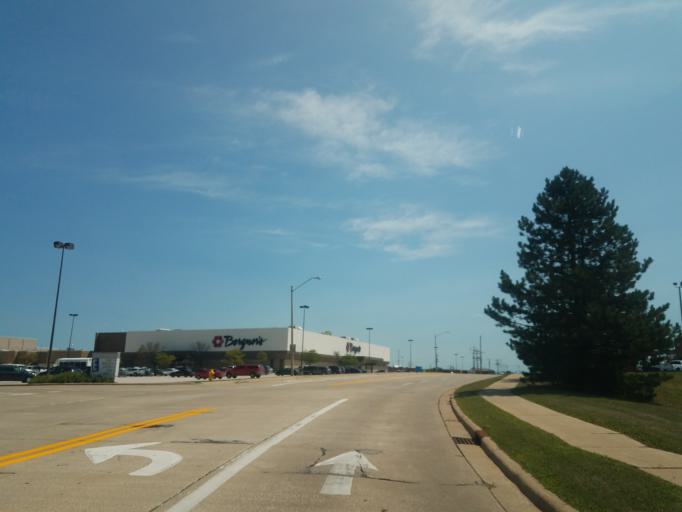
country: US
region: Illinois
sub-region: McLean County
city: Bloomington
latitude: 40.4840
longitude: -88.9582
